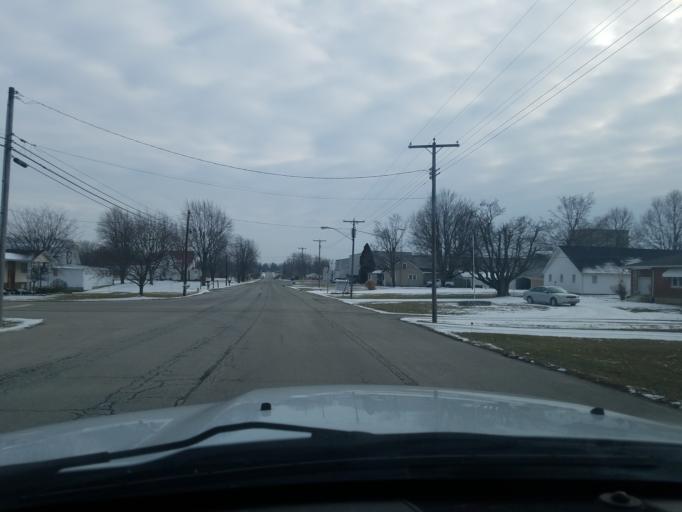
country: US
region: Indiana
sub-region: Randolph County
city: Winchester
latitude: 40.1896
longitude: -84.9816
